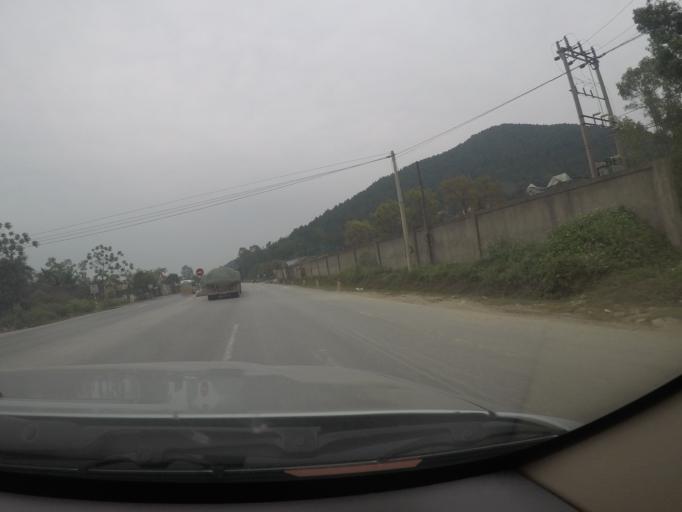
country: VN
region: Nghe An
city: Quan Hanh
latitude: 18.8684
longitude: 105.6240
